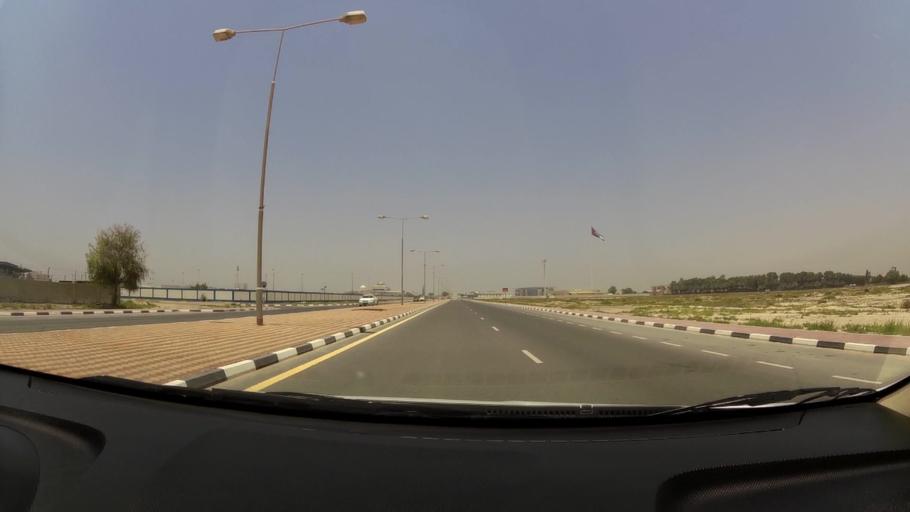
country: AE
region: Umm al Qaywayn
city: Umm al Qaywayn
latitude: 25.5638
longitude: 55.5608
